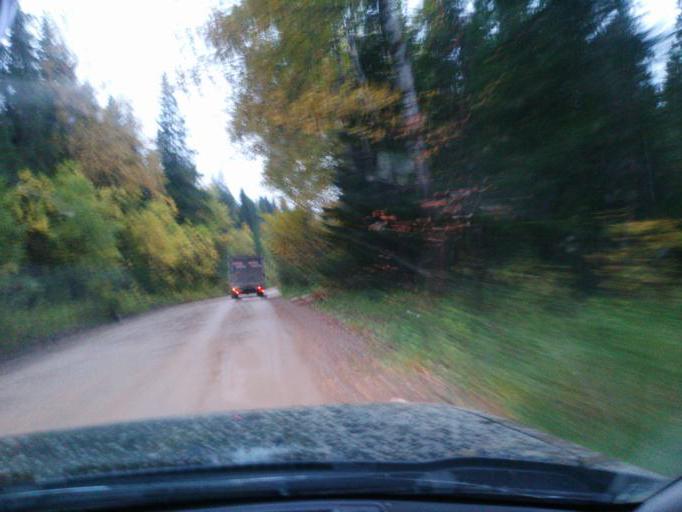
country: RU
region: Sverdlovsk
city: Sylva
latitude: 57.7985
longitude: 58.5683
